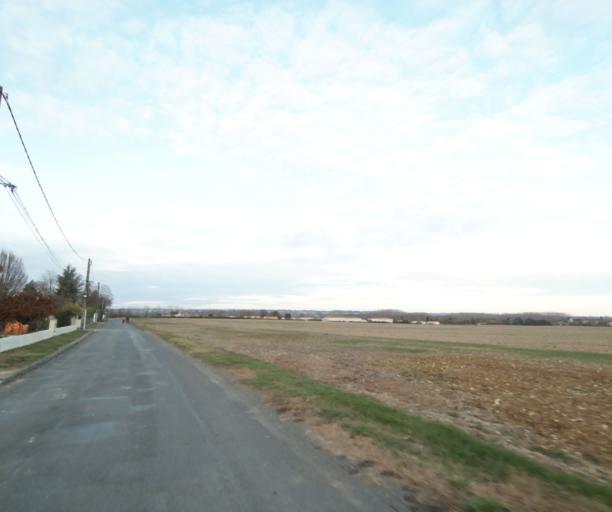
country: FR
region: Poitou-Charentes
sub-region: Departement de la Charente-Maritime
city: Les Gonds
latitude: 45.7136
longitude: -0.6294
